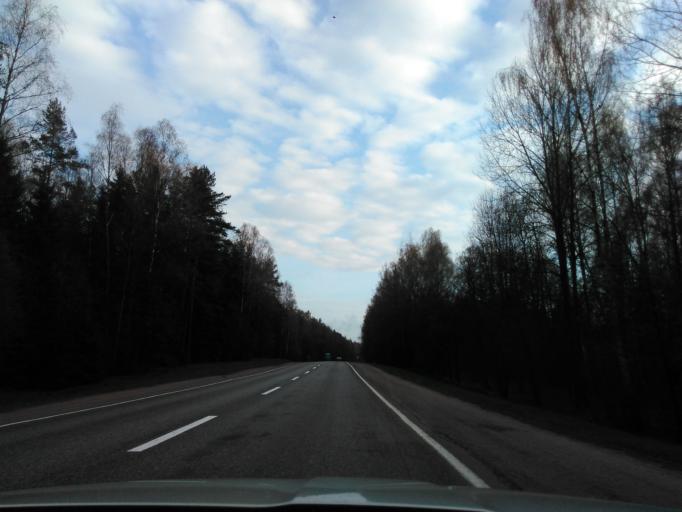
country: BY
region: Minsk
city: Lahoysk
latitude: 54.3132
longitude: 27.8756
